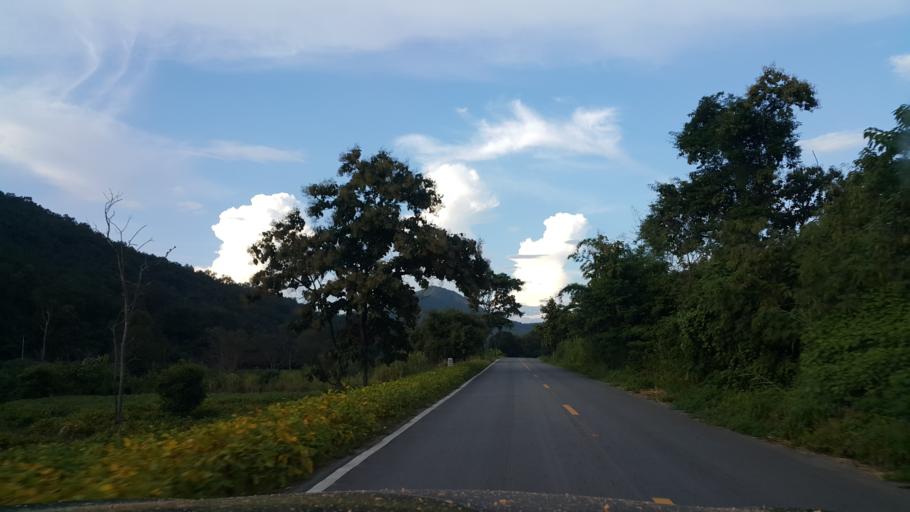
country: TH
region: Mae Hong Son
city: Mae Hi
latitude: 19.2319
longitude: 98.4439
